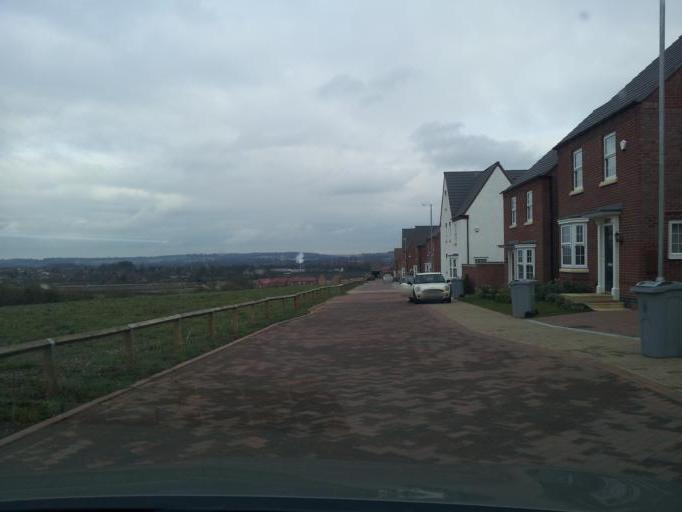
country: GB
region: England
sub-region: Lincolnshire
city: Great Gonerby
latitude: 52.9185
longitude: -0.6674
